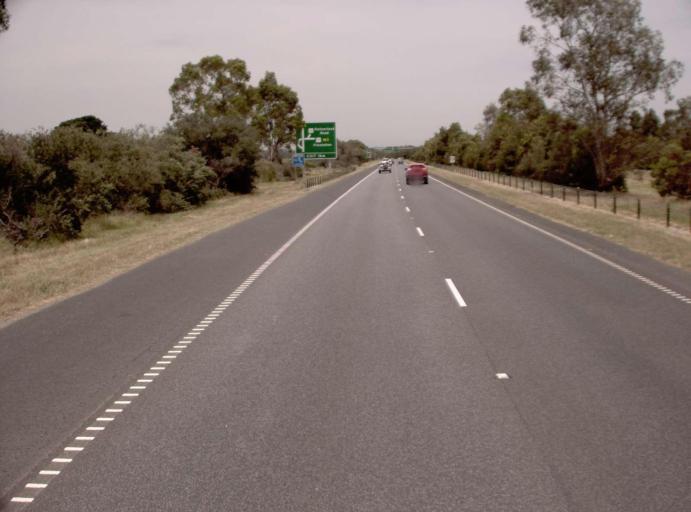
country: AU
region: Victoria
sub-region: Kingston
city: Patterson Lakes
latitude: -38.0750
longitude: 145.1503
